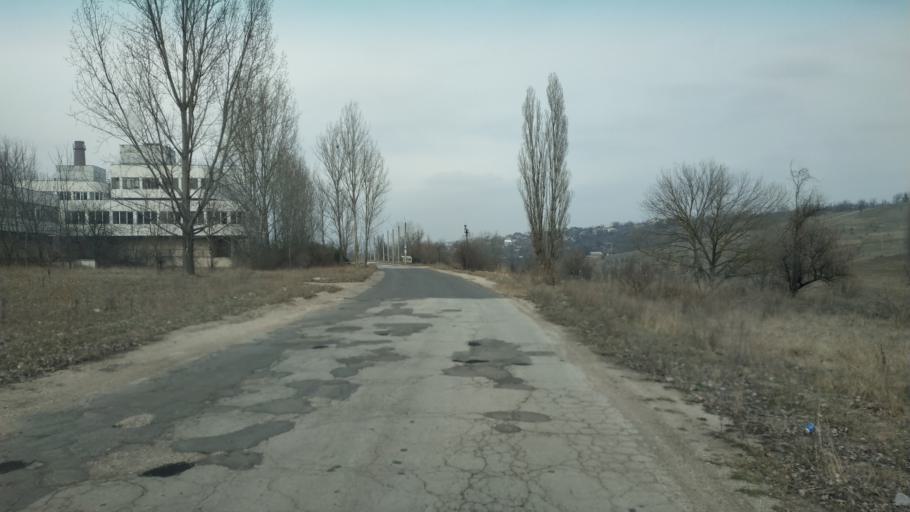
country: MD
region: Chisinau
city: Singera
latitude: 46.9022
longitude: 29.0199
